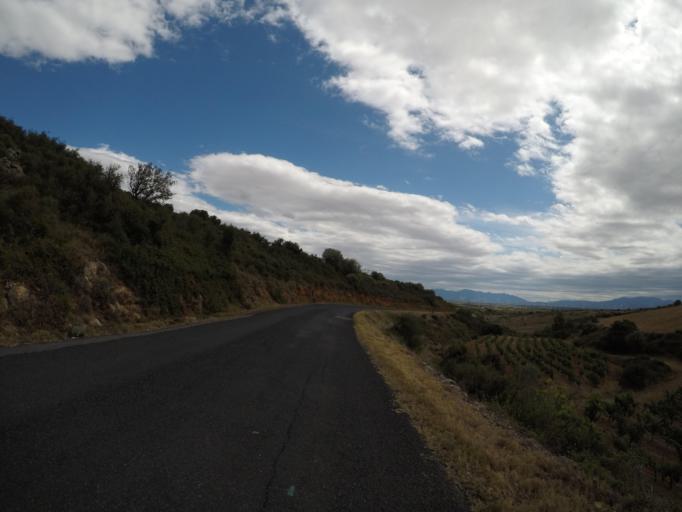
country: FR
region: Languedoc-Roussillon
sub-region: Departement des Pyrenees-Orientales
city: Baixas
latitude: 42.7532
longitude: 2.7769
